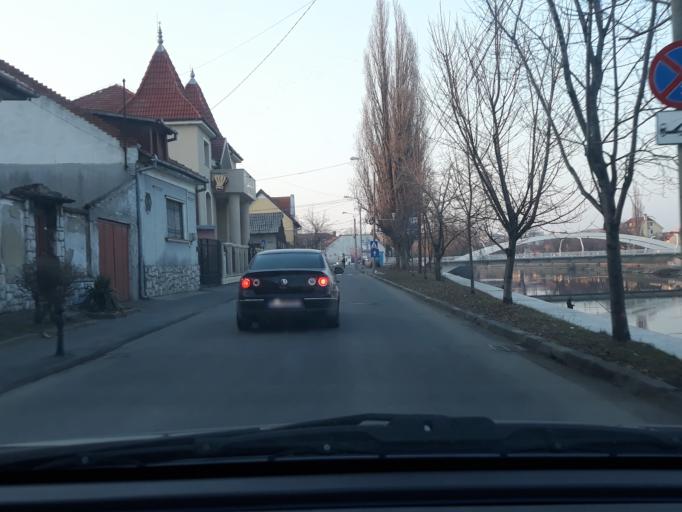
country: RO
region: Bihor
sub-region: Comuna Biharea
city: Oradea
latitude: 47.0592
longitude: 21.9259
